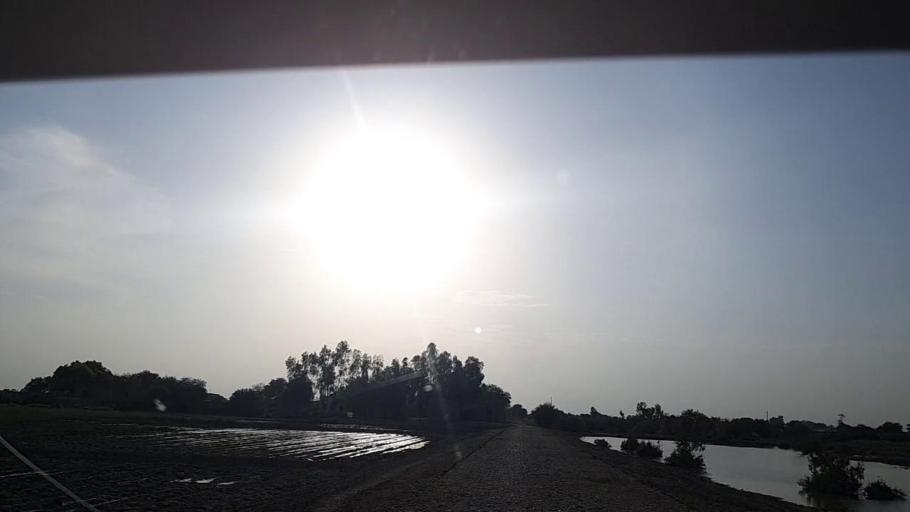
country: PK
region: Sindh
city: Khanpur
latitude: 27.8069
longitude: 69.3317
